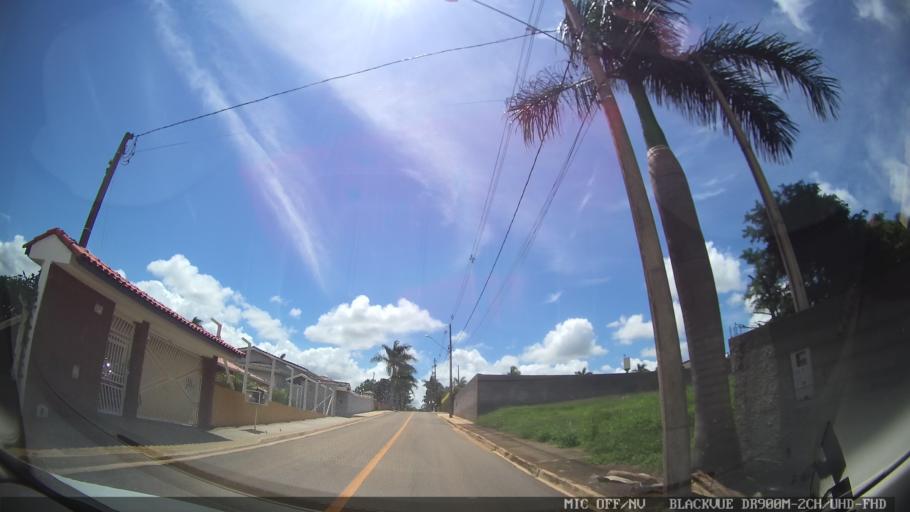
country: BR
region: Sao Paulo
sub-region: Amparo
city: Amparo
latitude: -22.8187
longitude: -46.6929
